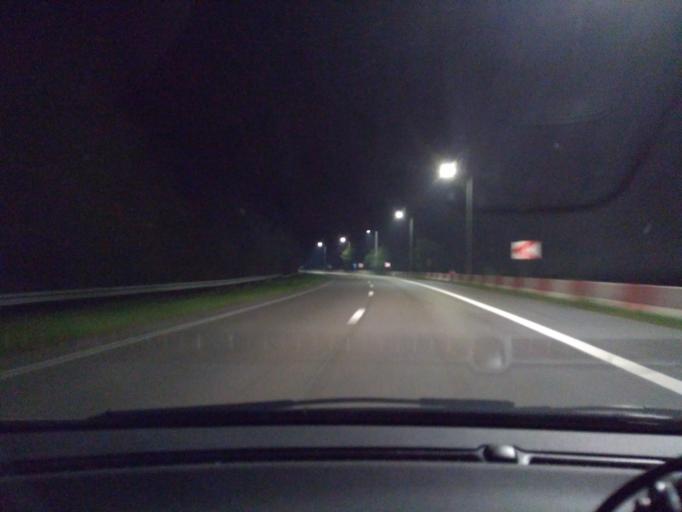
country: BE
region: Wallonia
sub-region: Province du Hainaut
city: Boussu
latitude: 50.4504
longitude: 3.7587
